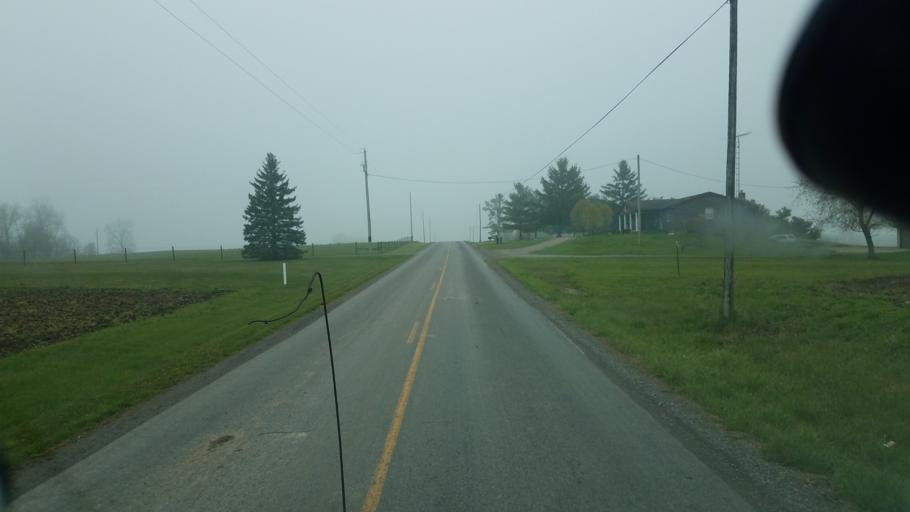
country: US
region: Ohio
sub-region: Logan County
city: De Graff
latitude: 40.3587
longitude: -83.9275
